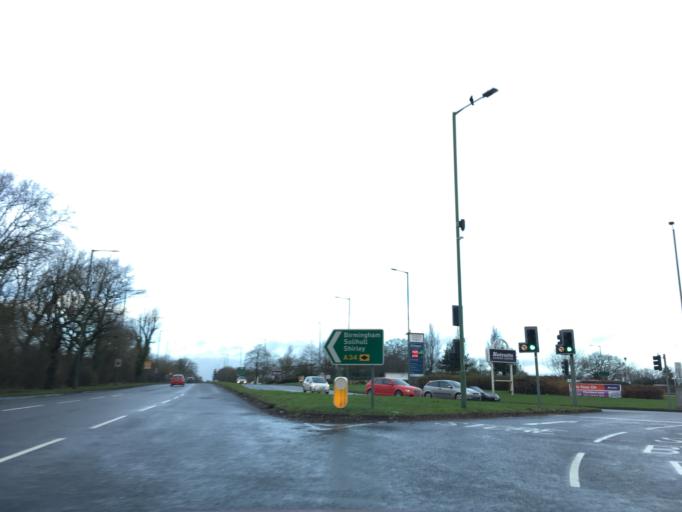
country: GB
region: England
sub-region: Solihull
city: Cheswick Green
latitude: 52.3814
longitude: -1.7903
